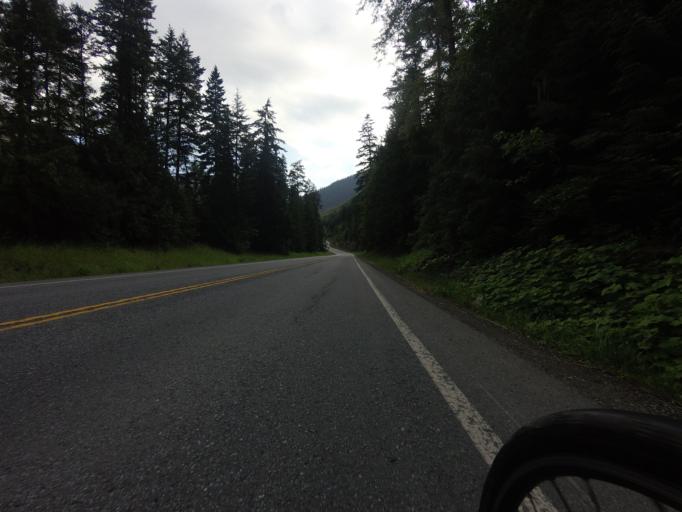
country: CA
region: British Columbia
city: Lillooet
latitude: 50.6271
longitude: -122.0982
